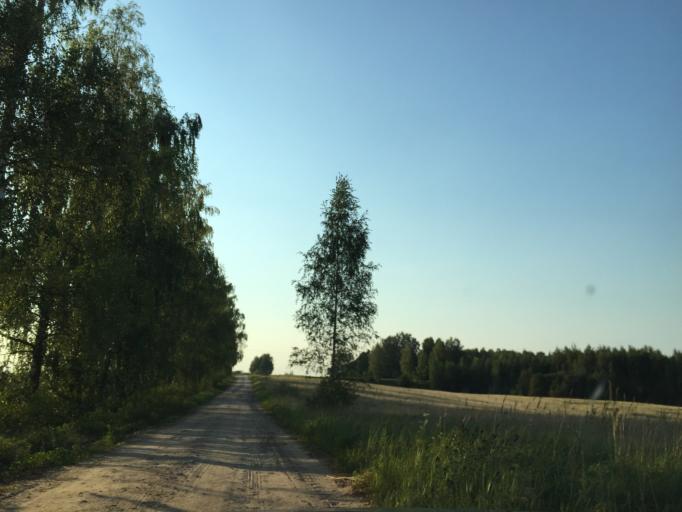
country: LV
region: Limbazu Rajons
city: Limbazi
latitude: 57.5575
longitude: 24.7669
